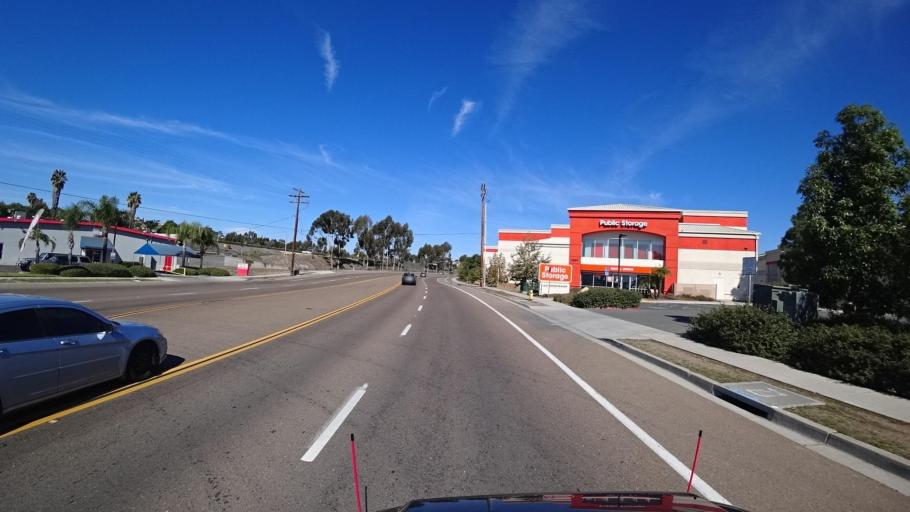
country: US
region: California
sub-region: San Diego County
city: La Presa
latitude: 32.7157
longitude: -117.0129
